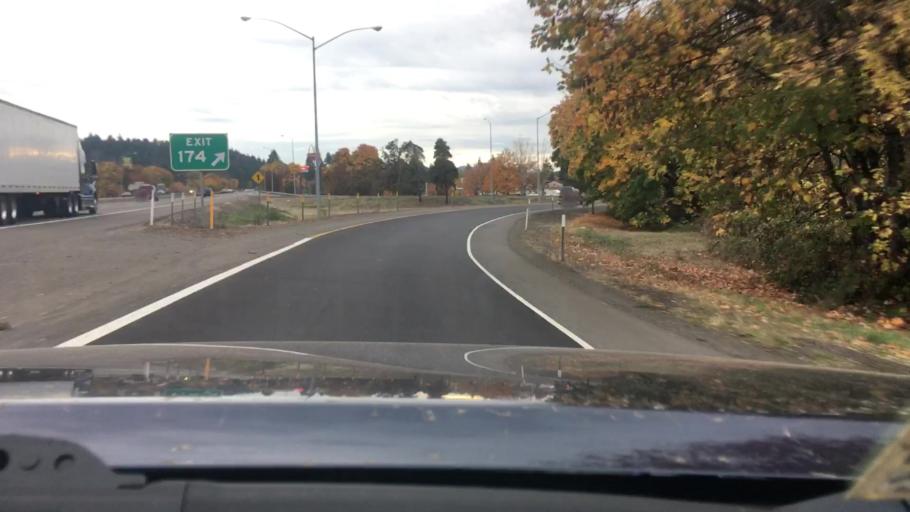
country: US
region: Oregon
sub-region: Lane County
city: Cottage Grove
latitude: 43.8053
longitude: -123.0388
